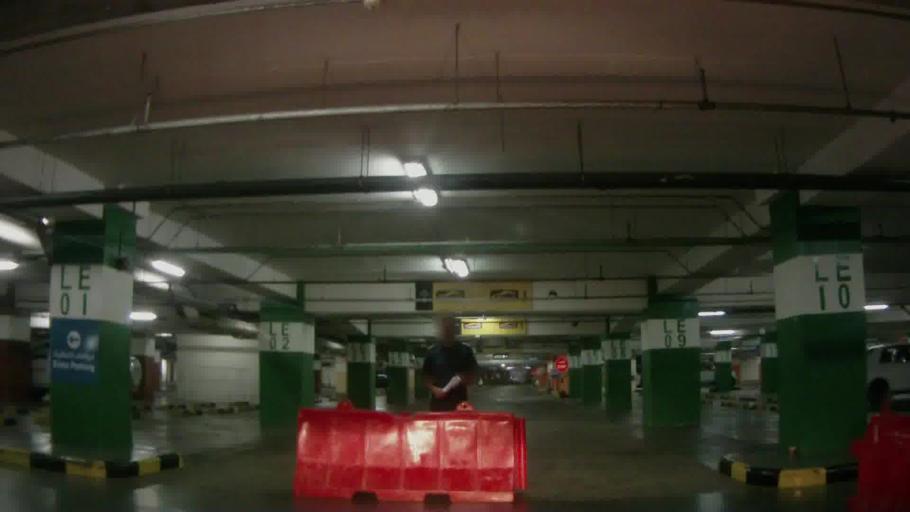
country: OM
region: Muhafazat Masqat
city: Bawshar
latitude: 23.5902
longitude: 58.4127
